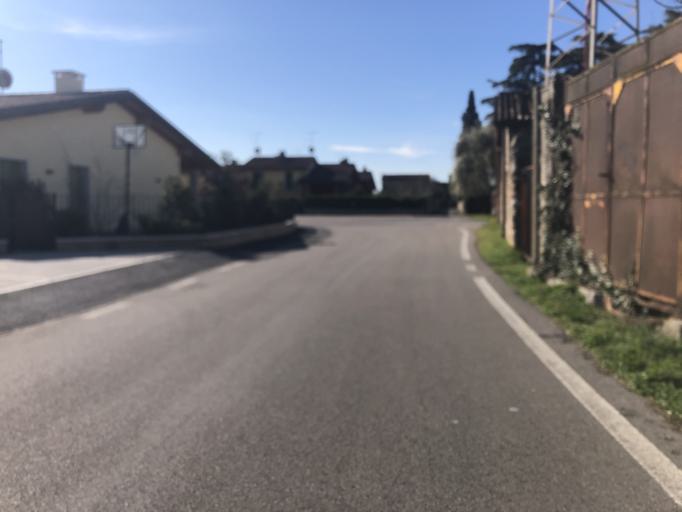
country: IT
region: Veneto
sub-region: Provincia di Verona
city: Ospedaletto
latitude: 45.5109
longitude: 10.8349
